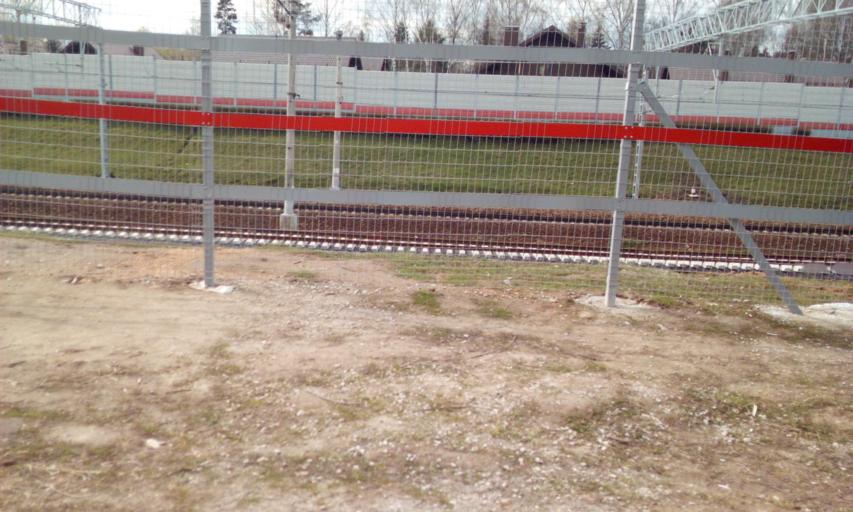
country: RU
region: Moscow
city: Novo-Peredelkino
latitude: 55.6485
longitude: 37.3335
